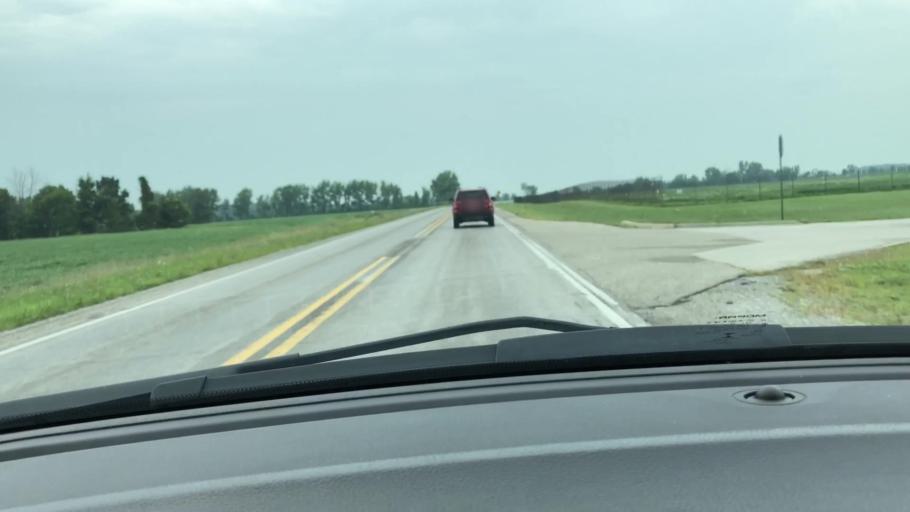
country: US
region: Michigan
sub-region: Saginaw County
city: Freeland
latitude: 43.5339
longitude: -84.0952
